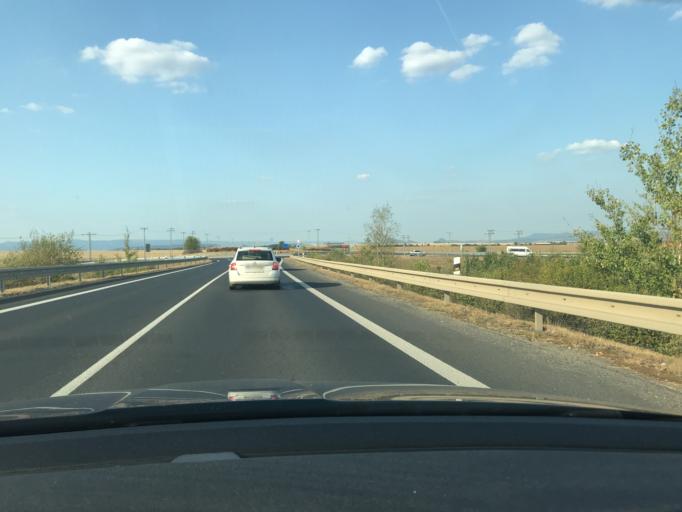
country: CZ
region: Ustecky
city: Zatec
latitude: 50.3849
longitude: 13.5551
